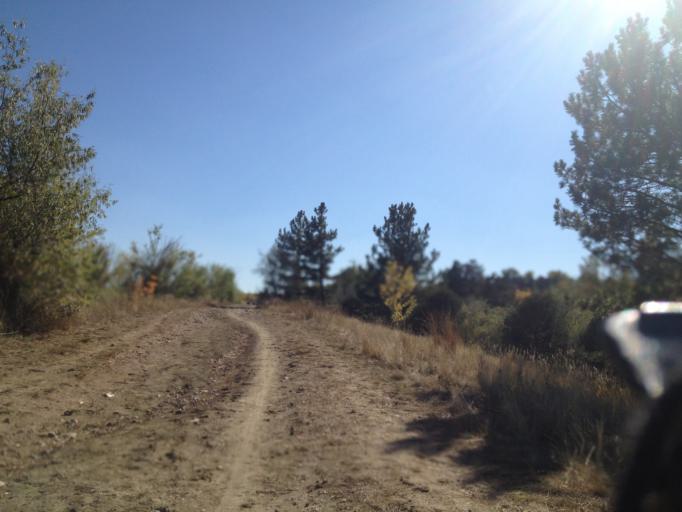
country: US
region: Colorado
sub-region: Boulder County
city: Boulder
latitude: 39.9804
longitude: -105.2353
